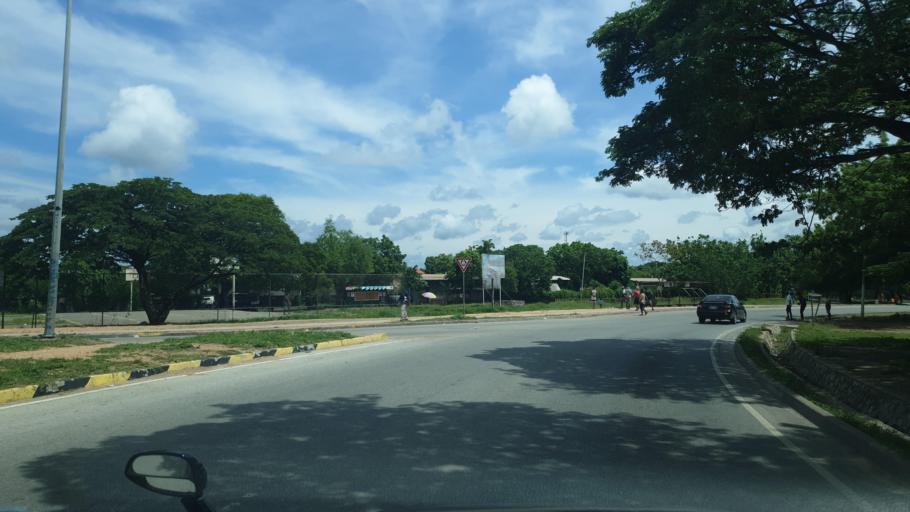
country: PG
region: National Capital
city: Port Moresby
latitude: -9.3969
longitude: 147.1583
